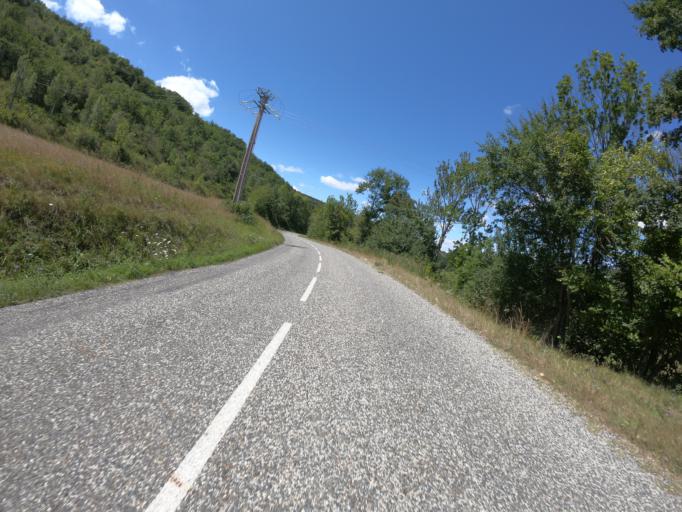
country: FR
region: Midi-Pyrenees
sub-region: Departement de l'Ariege
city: Mirepoix
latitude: 43.0441
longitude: 1.7701
